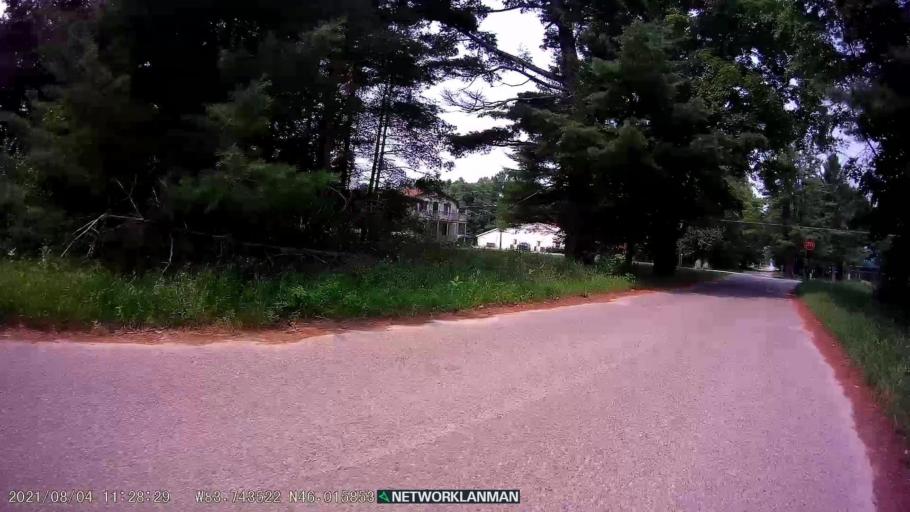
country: CA
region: Ontario
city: Thessalon
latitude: 46.0161
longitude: -83.7433
